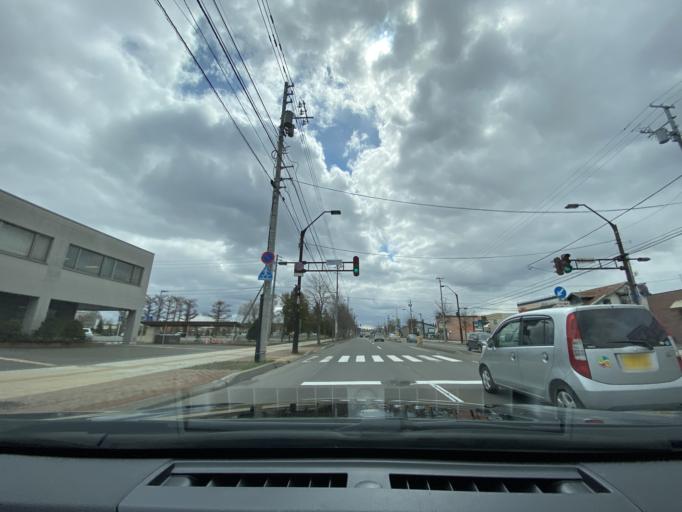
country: JP
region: Hokkaido
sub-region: Asahikawa-shi
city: Asahikawa
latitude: 43.7579
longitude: 142.3492
